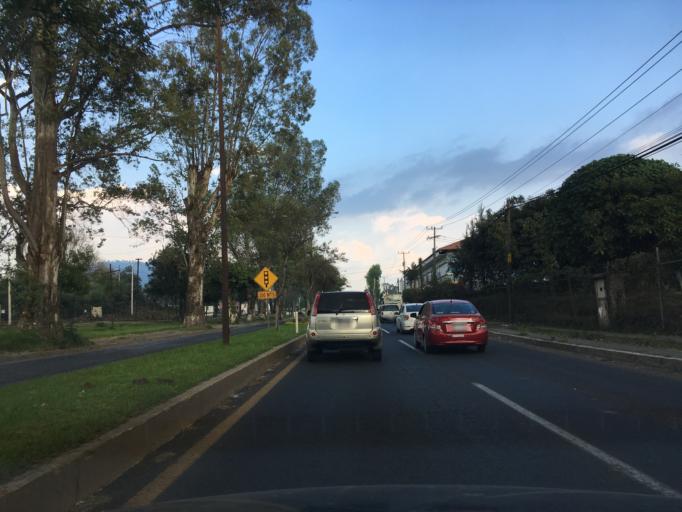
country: MX
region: Michoacan
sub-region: Uruapan
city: Toreo Bajo (El Toreo Bajo)
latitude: 19.4241
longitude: -102.0171
